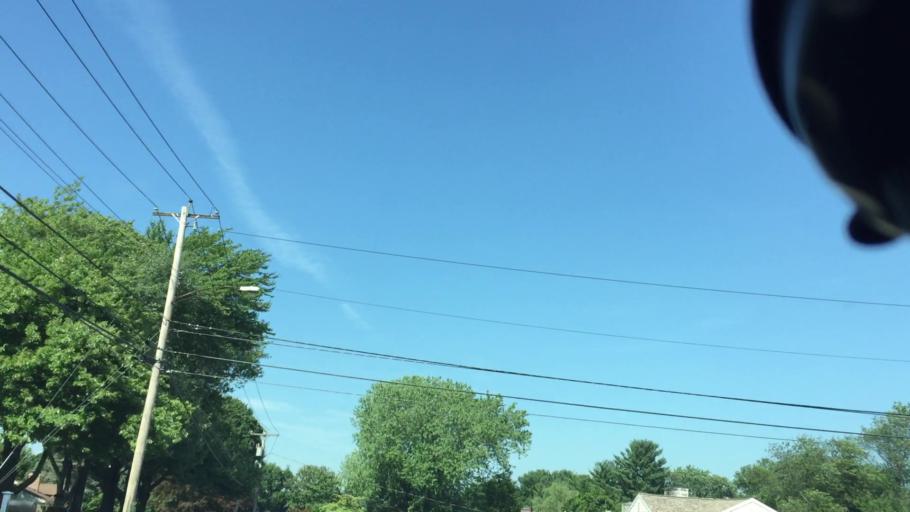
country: US
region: Connecticut
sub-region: Fairfield County
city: Trumbull
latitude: 41.2427
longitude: -73.2065
